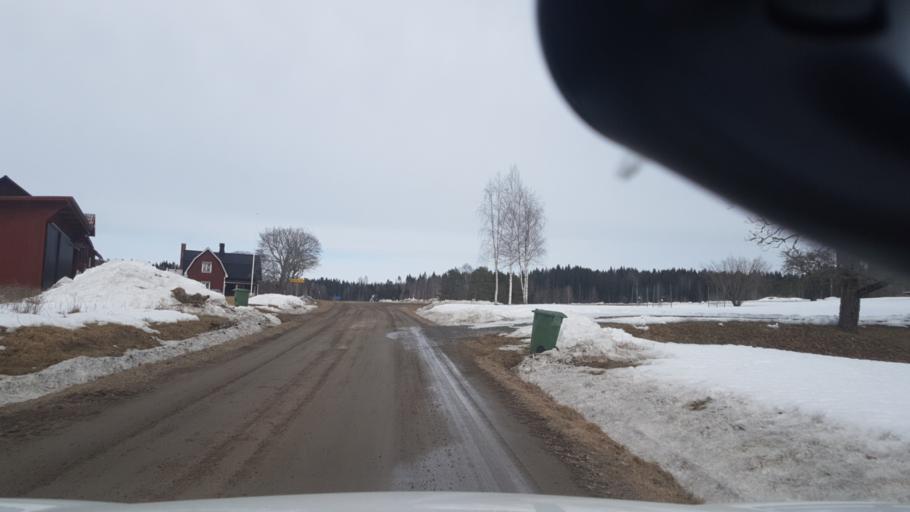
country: SE
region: Vaermland
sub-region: Eda Kommun
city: Amotfors
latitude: 59.7882
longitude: 12.4417
